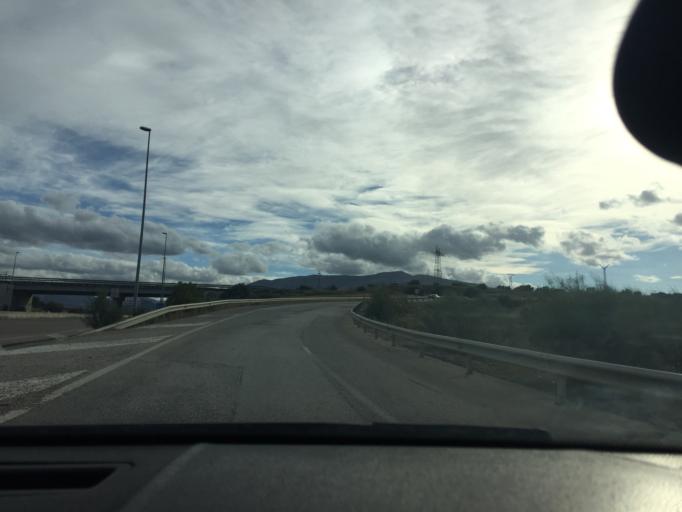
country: ES
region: Andalusia
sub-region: Provincia de Jaen
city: Jaen
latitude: 37.8115
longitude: -3.7746
